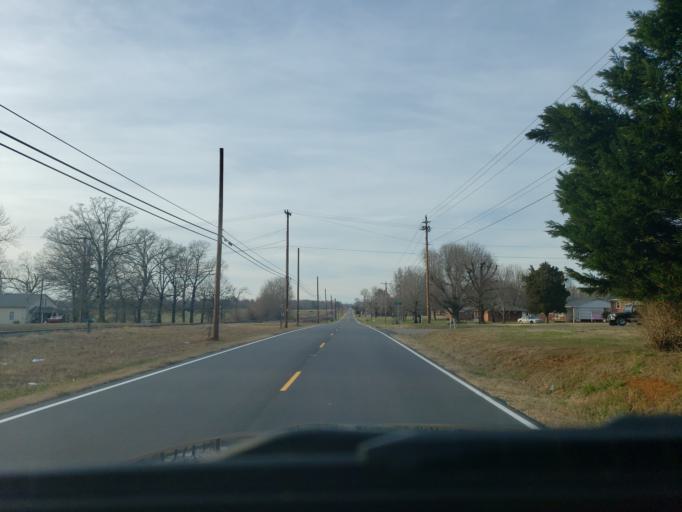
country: US
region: North Carolina
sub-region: Cleveland County
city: Boiling Springs
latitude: 35.3102
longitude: -81.7342
